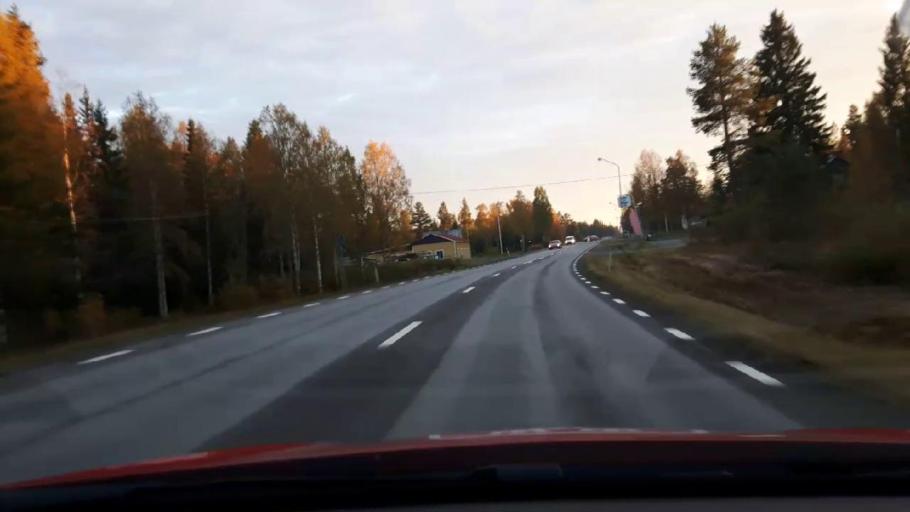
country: SE
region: Jaemtland
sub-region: OEstersunds Kommun
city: Lit
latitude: 63.2912
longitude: 14.8683
